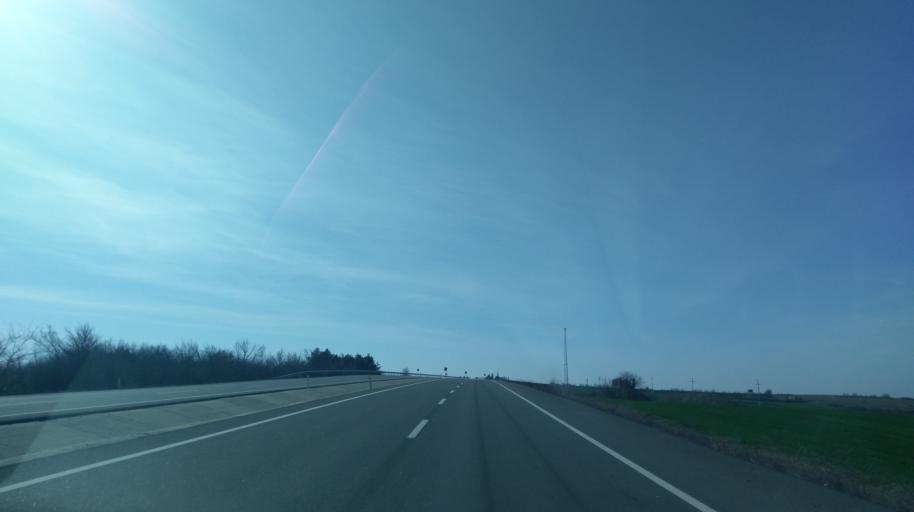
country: TR
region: Edirne
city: Hamidiye
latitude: 41.0829
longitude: 26.6397
